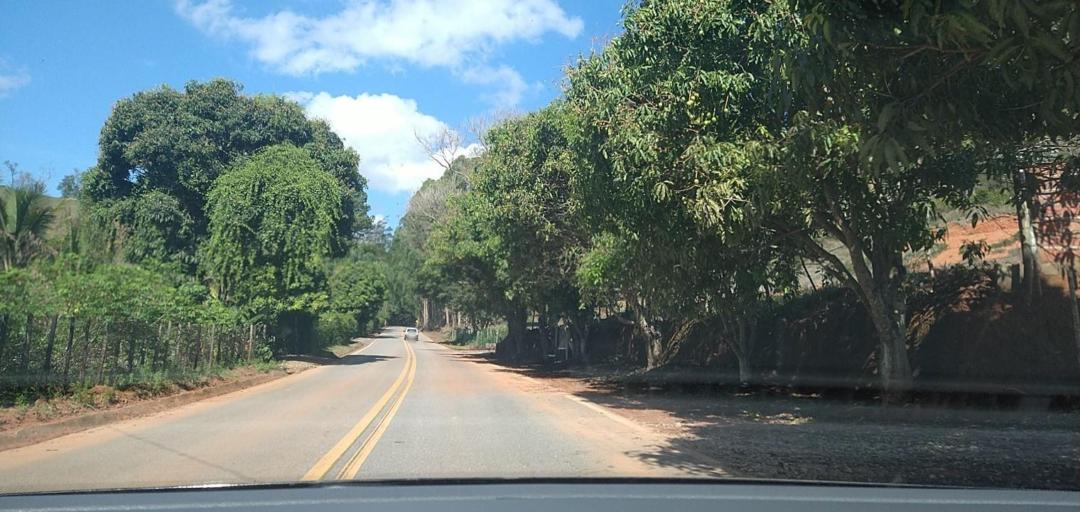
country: BR
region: Minas Gerais
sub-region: Alvinopolis
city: Alvinopolis
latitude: -20.0359
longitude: -43.0406
